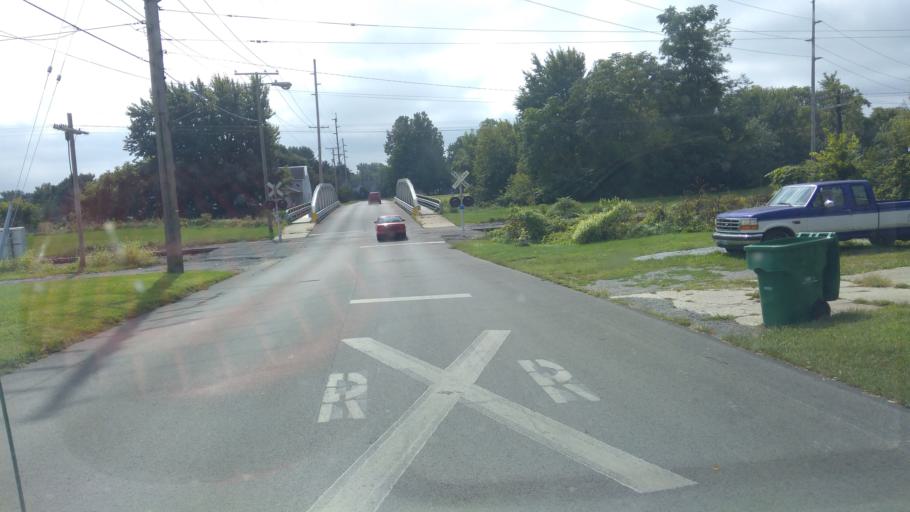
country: US
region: Ohio
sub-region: Hardin County
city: Kenton
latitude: 40.6451
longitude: -83.6134
